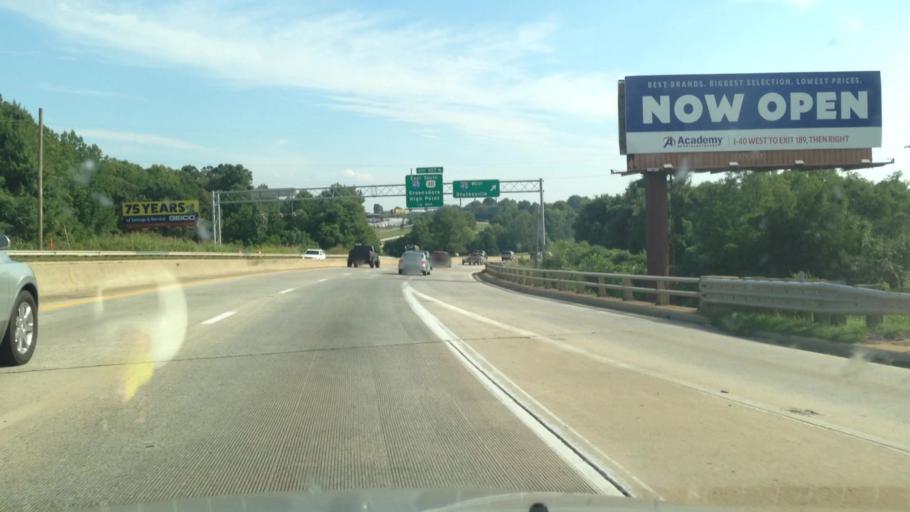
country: US
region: North Carolina
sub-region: Forsyth County
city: Winston-Salem
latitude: 36.0667
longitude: -80.2291
